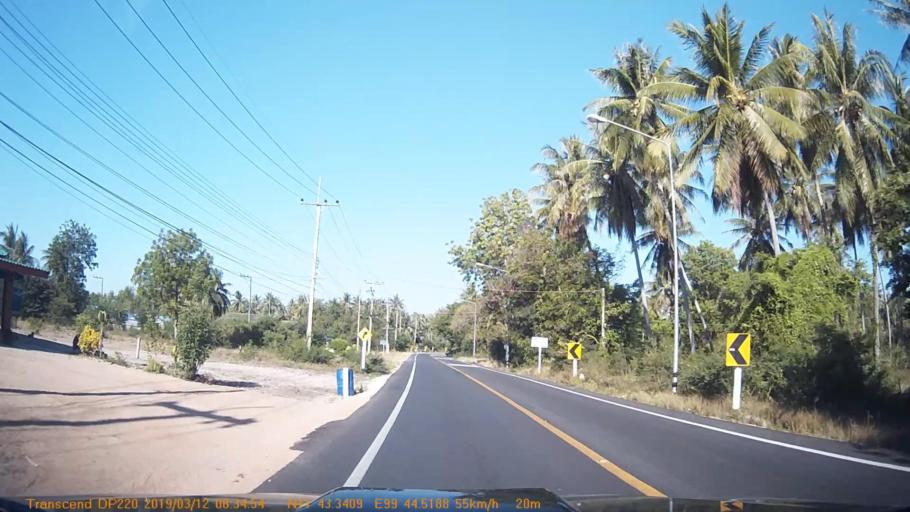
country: TH
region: Prachuap Khiri Khan
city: Prachuap Khiri Khan
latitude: 11.7225
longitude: 99.7416
